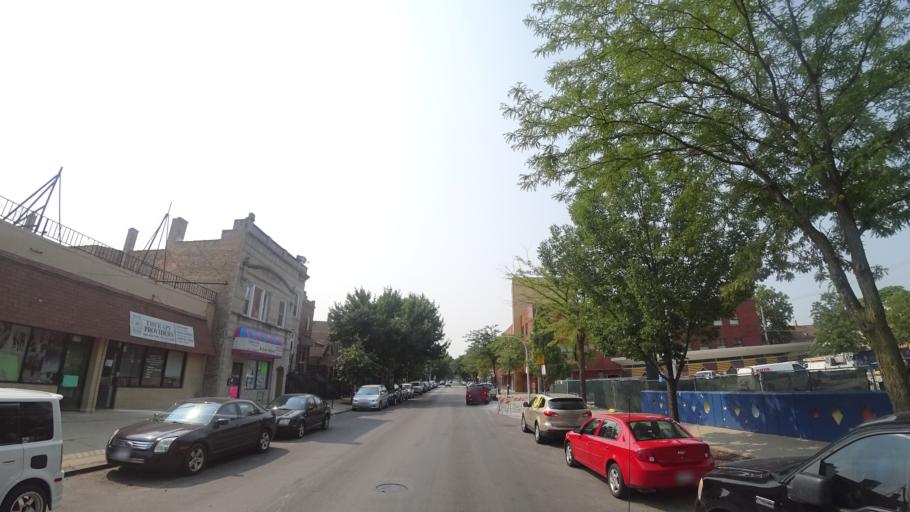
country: US
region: Illinois
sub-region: Cook County
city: Cicero
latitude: 41.8438
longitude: -87.7173
